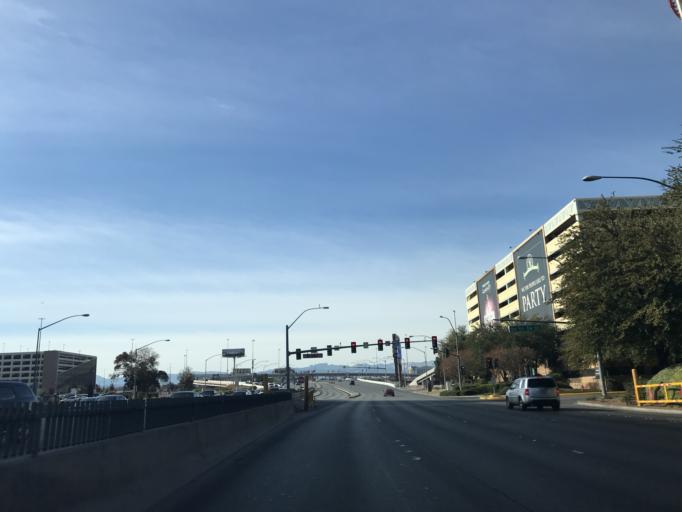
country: US
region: Nevada
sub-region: Clark County
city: Paradise
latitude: 36.1009
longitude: -115.1753
